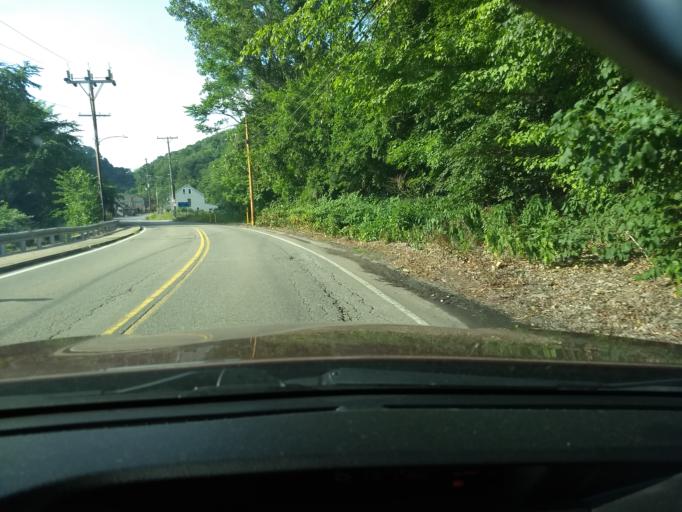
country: US
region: Pennsylvania
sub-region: Westmoreland County
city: Arnold
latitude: 40.5897
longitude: -79.7766
